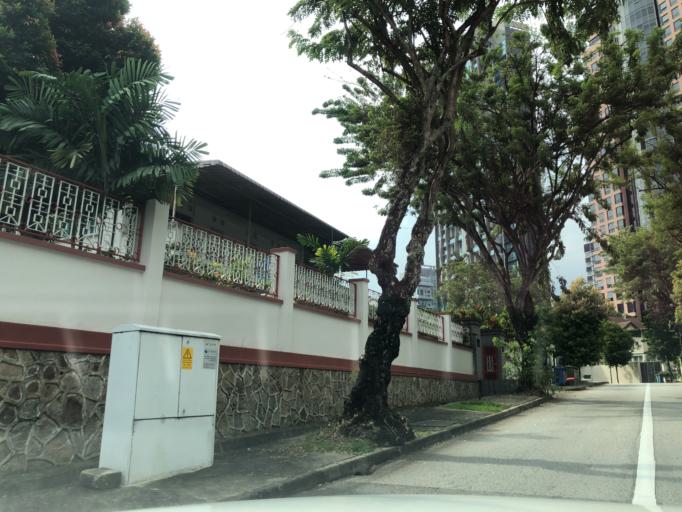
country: SG
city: Singapore
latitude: 1.3023
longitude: 103.8288
